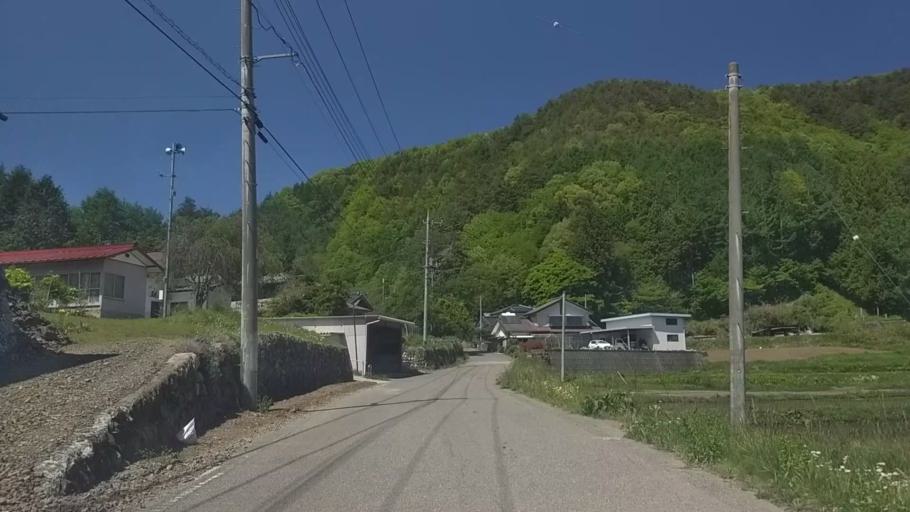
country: JP
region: Yamanashi
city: Nirasaki
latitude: 35.8753
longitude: 138.4535
